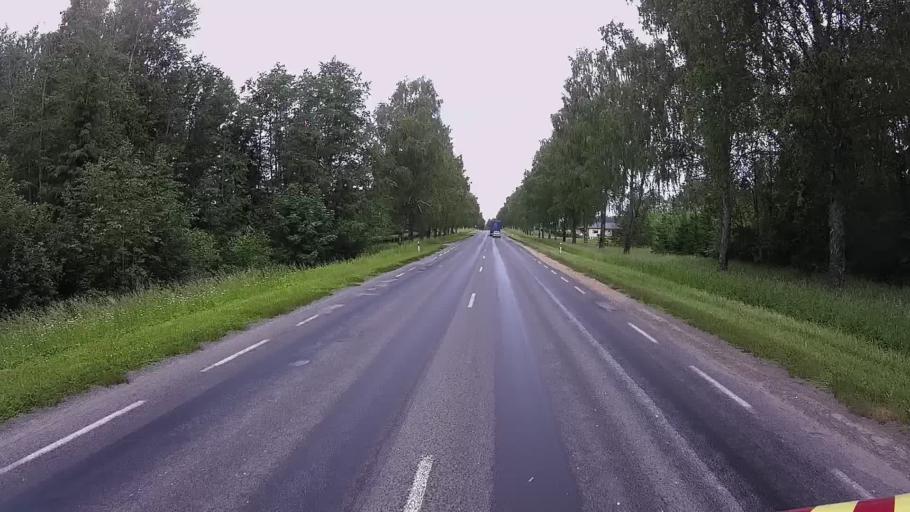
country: EE
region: Viljandimaa
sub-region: Viljandi linn
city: Viljandi
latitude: 58.3050
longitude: 25.5738
